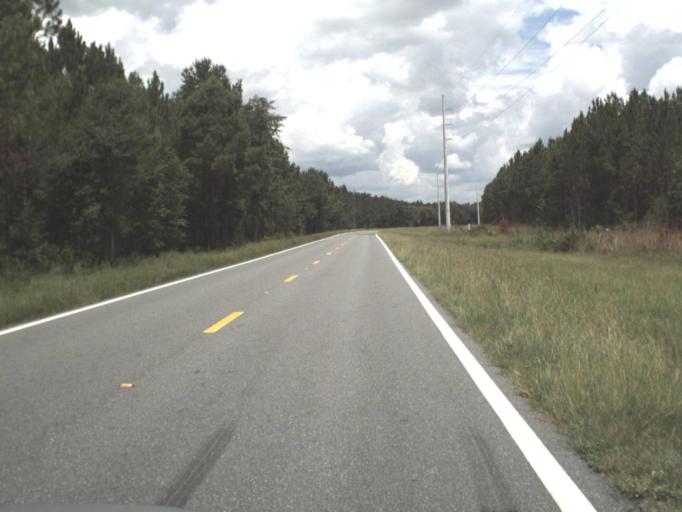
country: US
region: Florida
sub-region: Union County
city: Lake Butler
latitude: 29.9196
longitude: -82.4054
